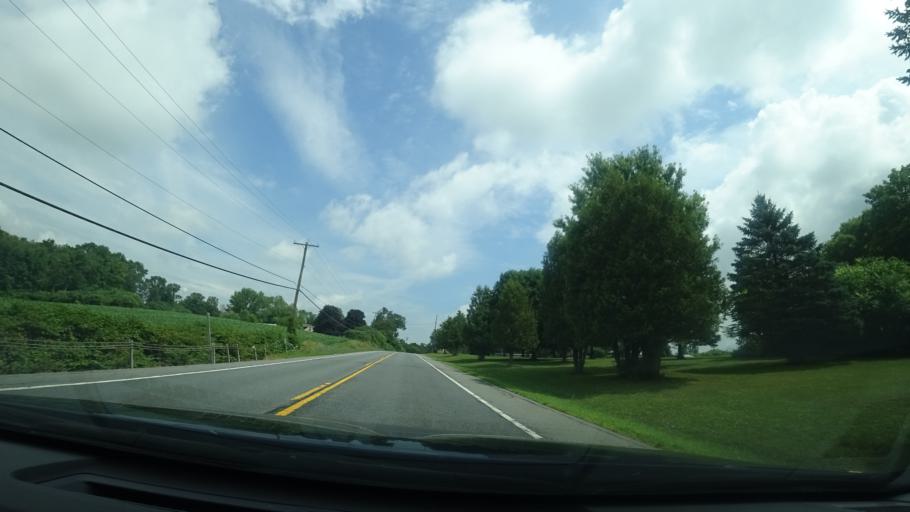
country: US
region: New York
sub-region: Washington County
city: Hudson Falls
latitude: 43.3396
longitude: -73.5529
